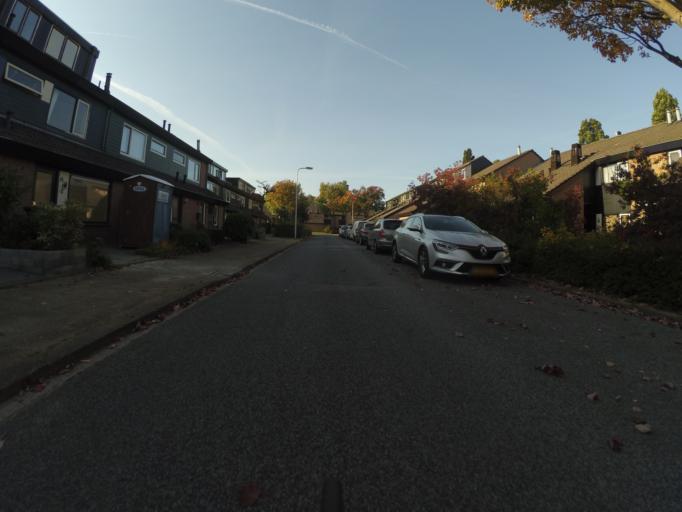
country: NL
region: Utrecht
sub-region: Gemeente Bunnik
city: Bunnik
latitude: 52.0820
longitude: 5.2126
